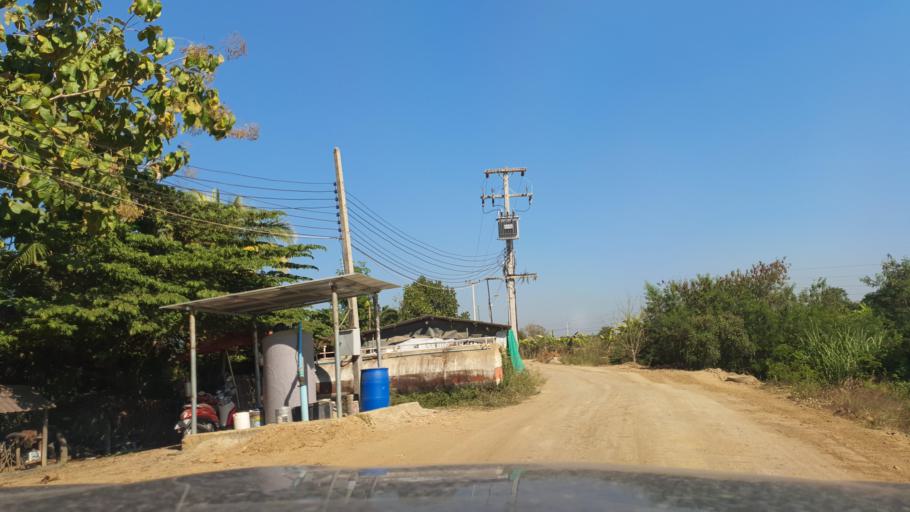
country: TH
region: Chiang Mai
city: Saraphi
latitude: 18.7173
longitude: 99.0779
